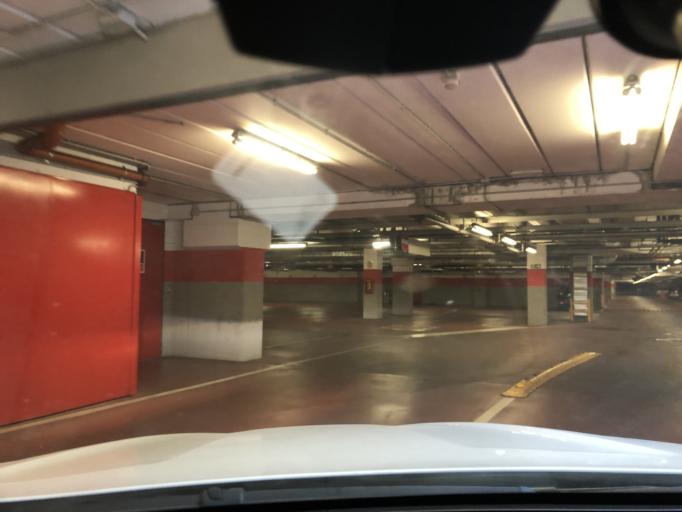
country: IT
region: Lombardy
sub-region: Citta metropolitana di Milano
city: Bresso
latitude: 45.5118
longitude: 9.1732
